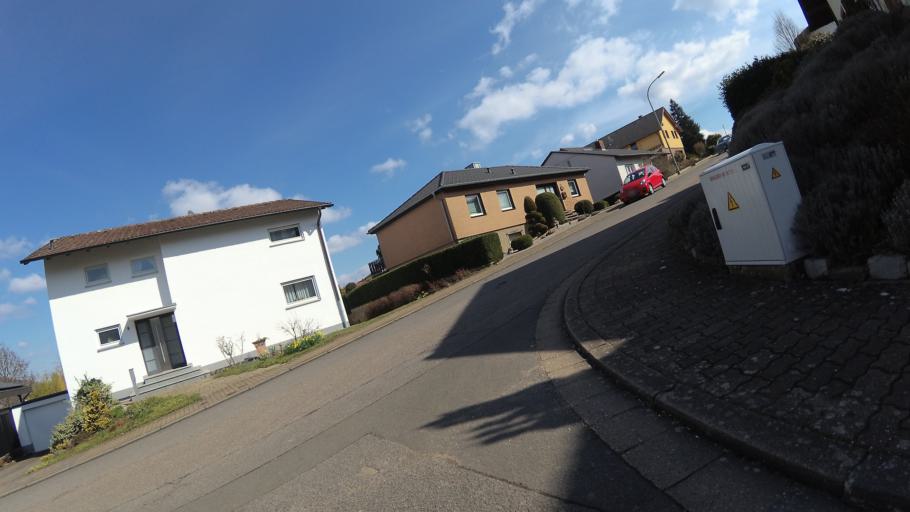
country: DE
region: Saarland
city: Rehlingen-Siersburg
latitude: 49.3568
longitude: 6.6625
